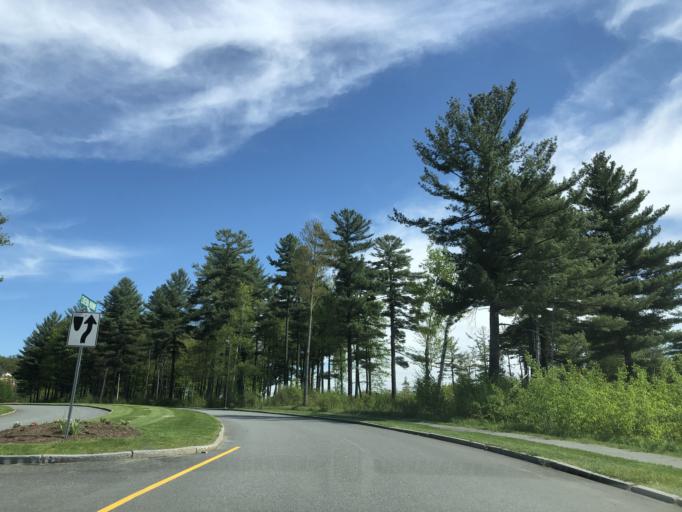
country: US
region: New Hampshire
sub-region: Grafton County
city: Hanover
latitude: 43.6768
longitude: -72.2640
